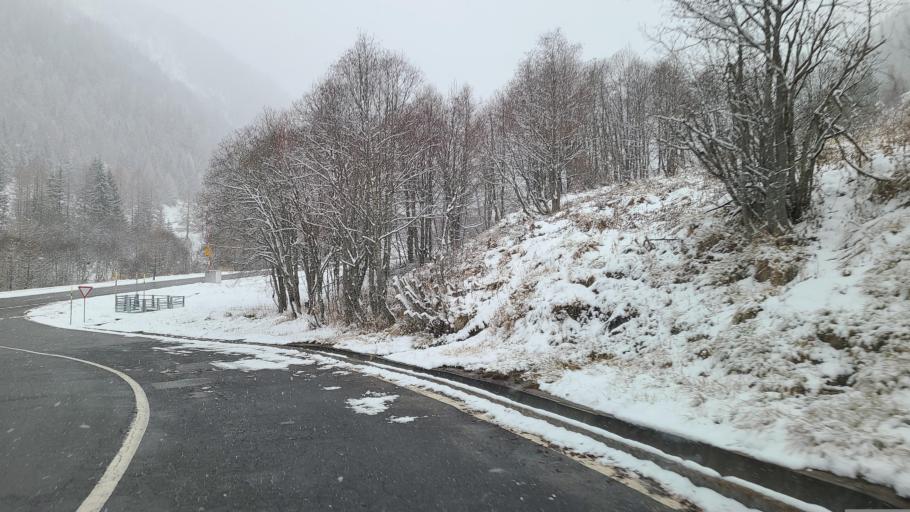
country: CH
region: Ticino
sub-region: Leventina District
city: Airolo
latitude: 46.5042
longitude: 8.5089
